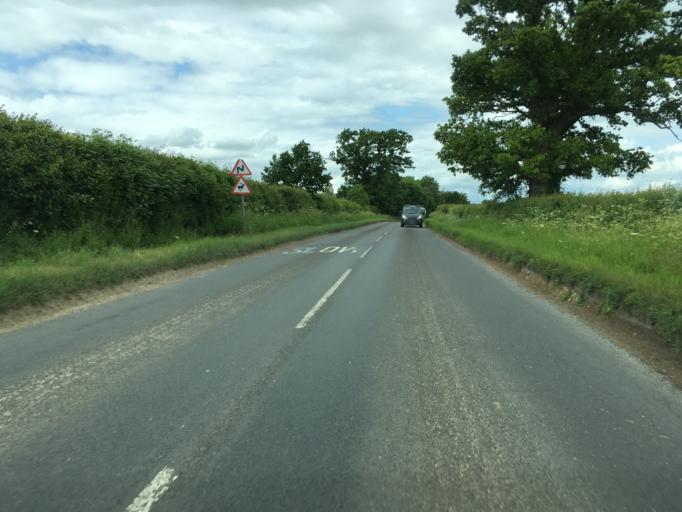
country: GB
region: England
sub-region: Gloucestershire
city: Cirencester
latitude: 51.6857
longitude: -1.9693
